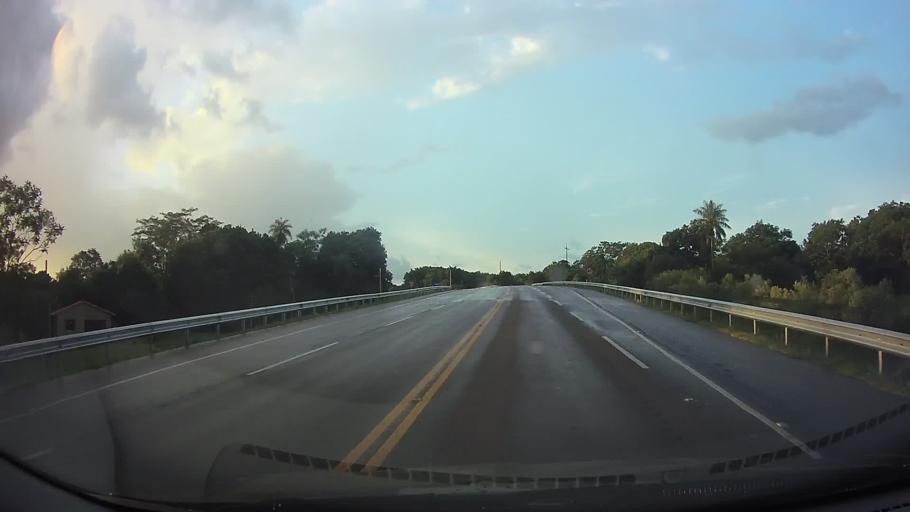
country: PY
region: Paraguari
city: Paraguari
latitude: -25.6052
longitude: -57.1868
